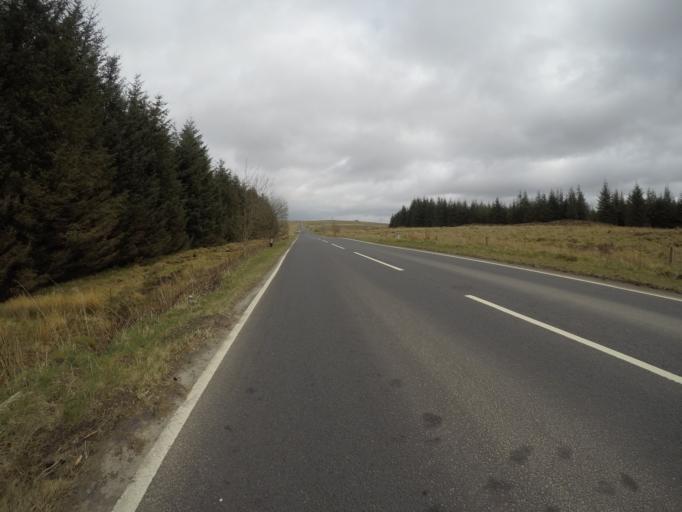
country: GB
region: Scotland
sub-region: East Renfrewshire
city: Newton Mearns
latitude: 55.7061
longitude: -4.3655
